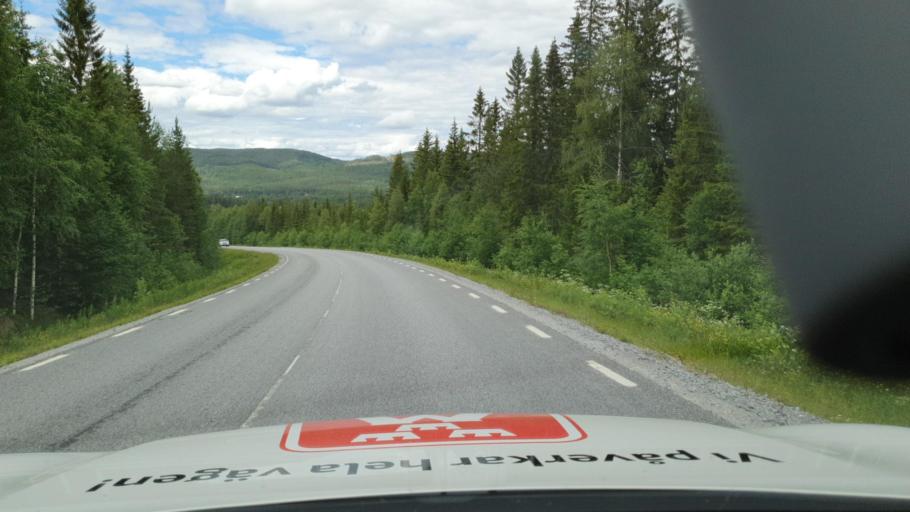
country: SE
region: Vaesterbotten
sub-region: Bjurholms Kommun
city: Bjurholm
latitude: 63.9057
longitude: 19.0903
